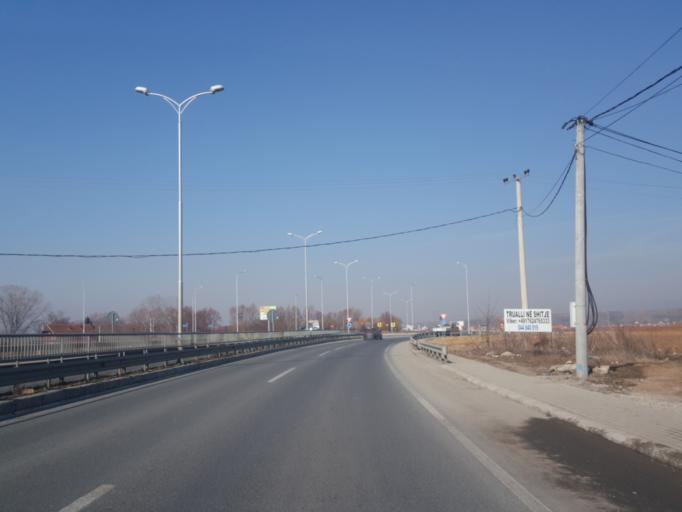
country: XK
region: Pristina
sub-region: Komuna e Obiliqit
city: Obiliq
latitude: 42.7249
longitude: 21.0807
